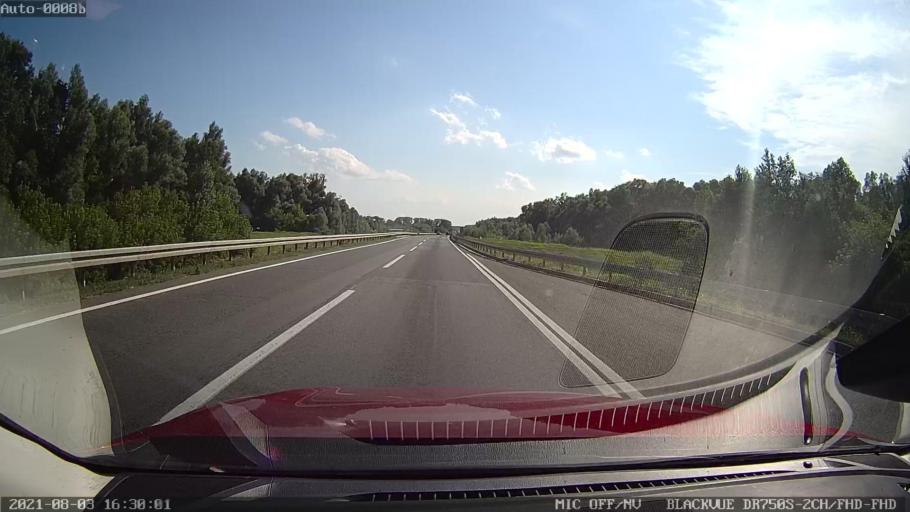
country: HR
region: Osjecko-Baranjska
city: Visnjevac
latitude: 45.5883
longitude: 18.6503
